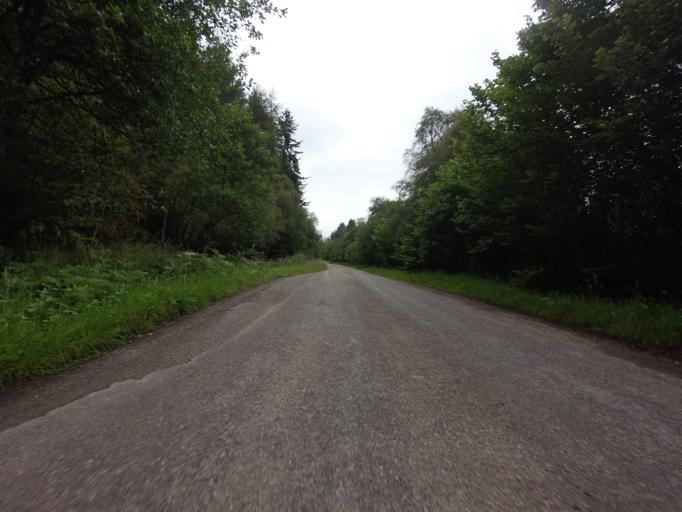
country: GB
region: Scotland
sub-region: Highland
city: Evanton
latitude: 57.9650
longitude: -4.4110
